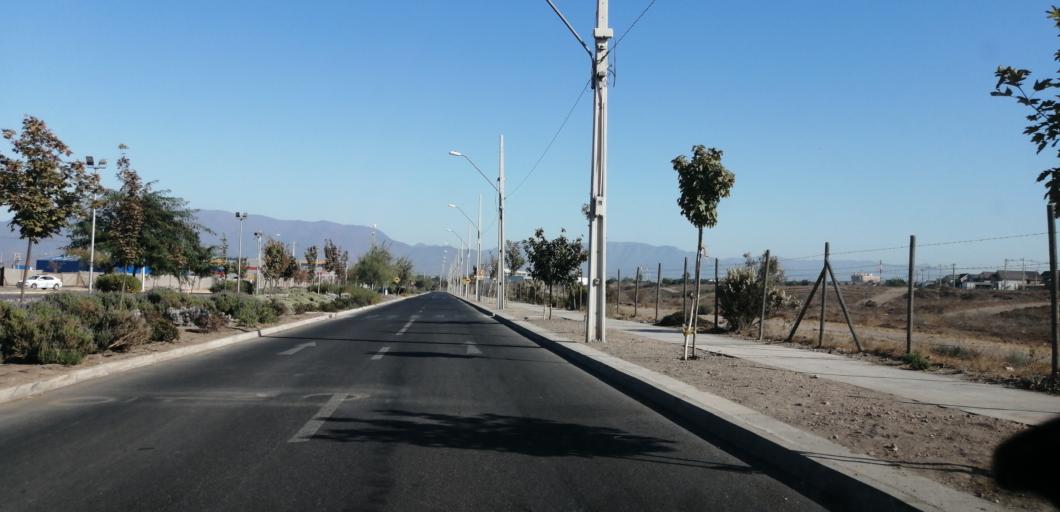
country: CL
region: Santiago Metropolitan
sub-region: Provincia de Santiago
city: Lo Prado
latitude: -33.4386
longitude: -70.7779
